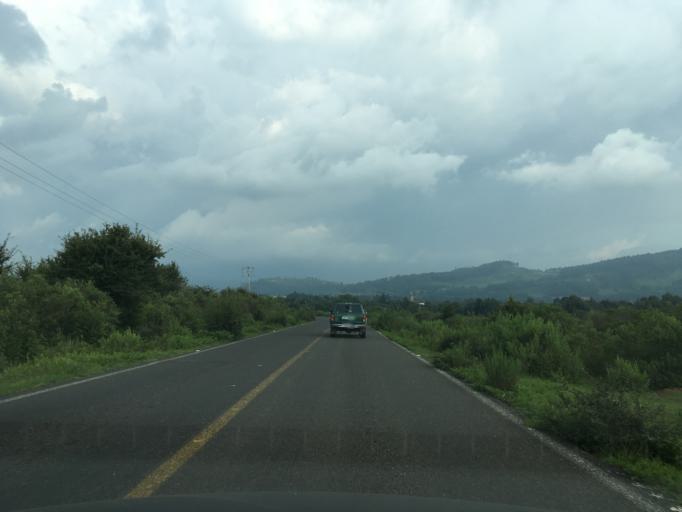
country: MX
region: Michoacan
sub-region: Patzcuaro
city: Santa Maria Huiramangaro (San Juan Tumbio)
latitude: 19.5200
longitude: -101.7707
